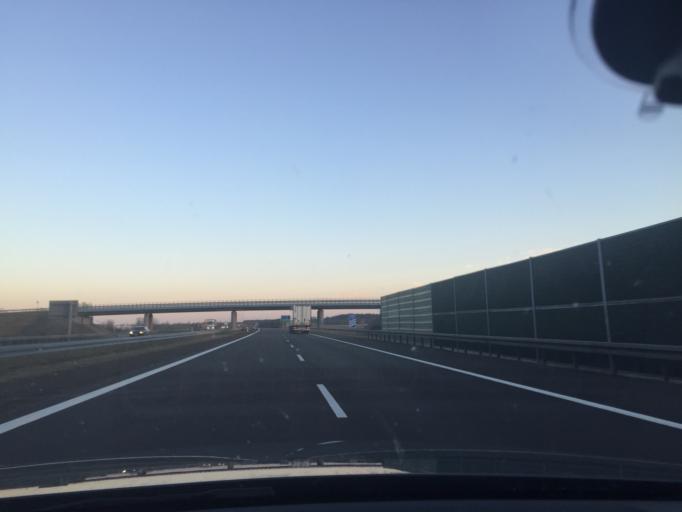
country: PL
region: Greater Poland Voivodeship
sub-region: Powiat kolski
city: Dabie
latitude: 52.0755
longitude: 18.8058
